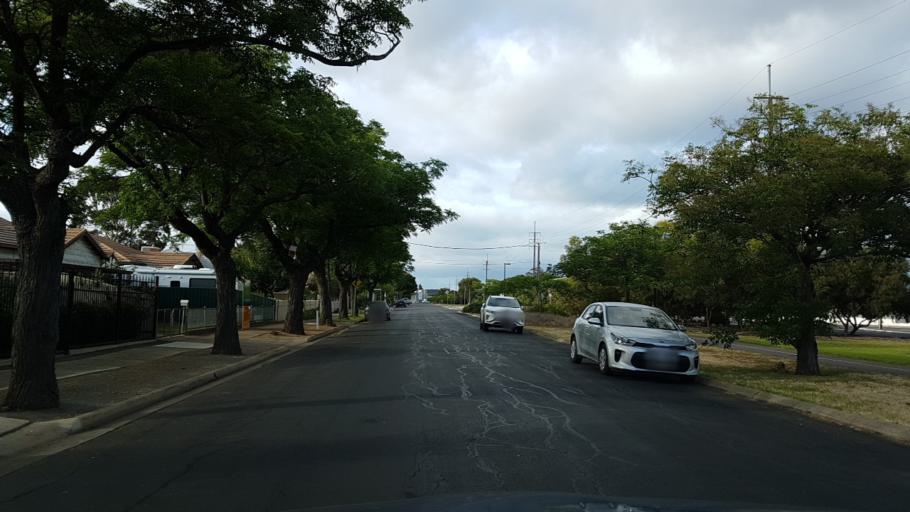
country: AU
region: South Australia
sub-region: Unley
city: Forestville
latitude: -34.9439
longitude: 138.5668
